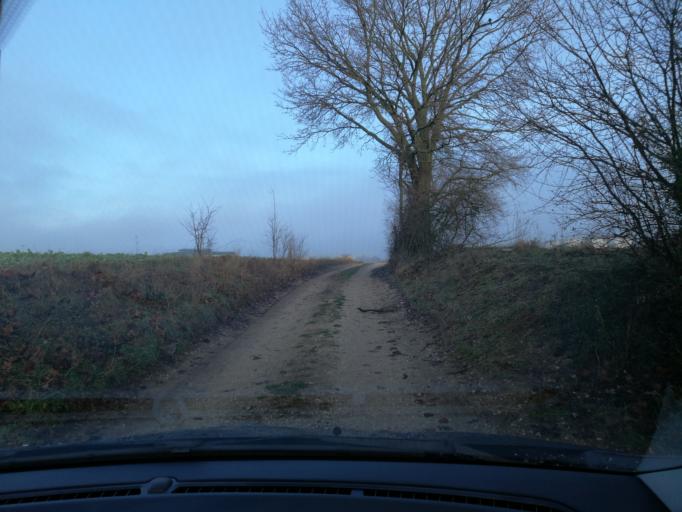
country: DE
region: Bavaria
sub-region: Regierungsbezirk Mittelfranken
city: Furth
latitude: 49.4911
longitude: 10.9486
